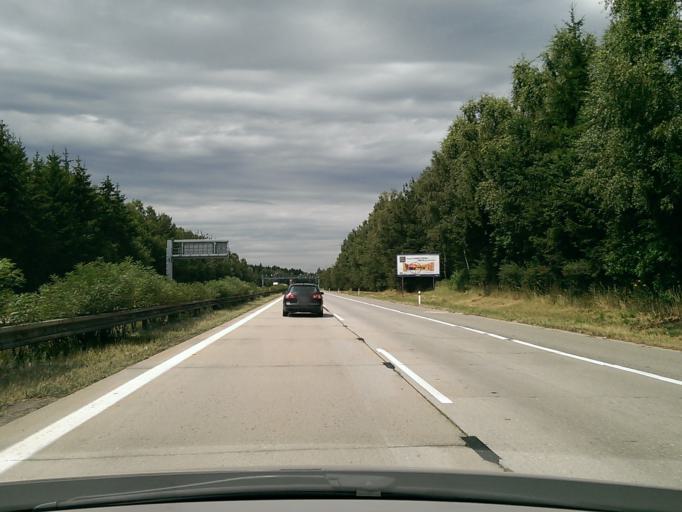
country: CZ
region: Vysocina
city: Luka nad Jihlavou
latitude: 49.4115
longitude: 15.7292
